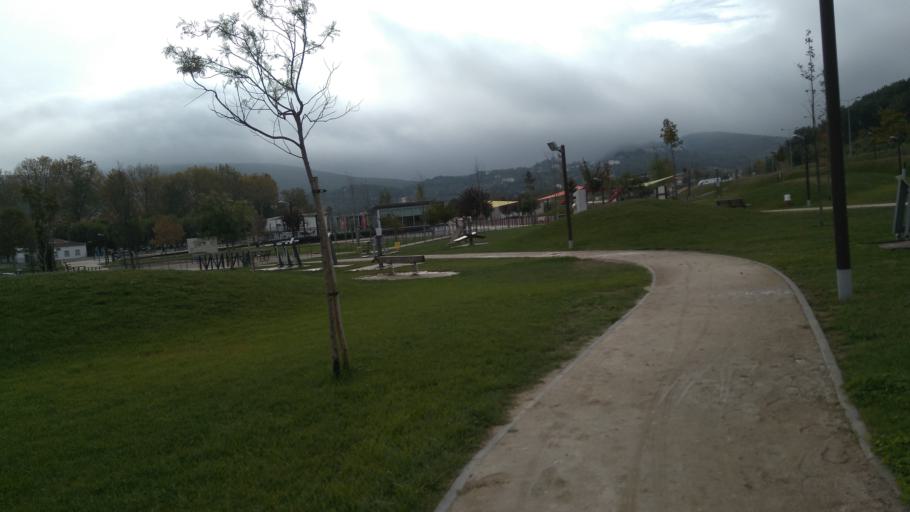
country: PT
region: Leiria
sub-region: Porto de Mos
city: Porto de Mos
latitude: 39.5993
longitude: -8.8221
